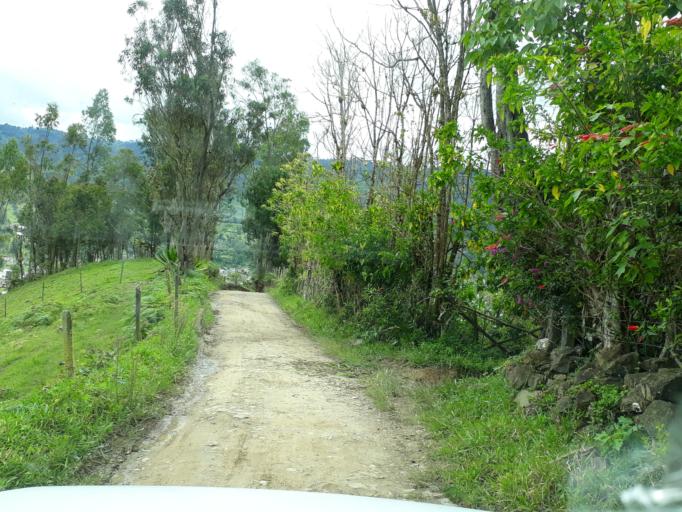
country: CO
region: Cundinamarca
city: Gacheta
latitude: 4.8092
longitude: -73.6444
